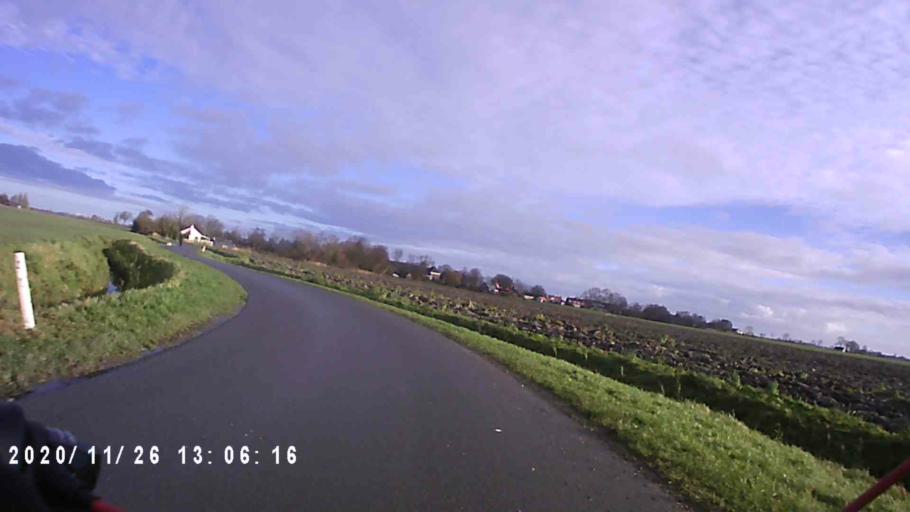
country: NL
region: Groningen
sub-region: Gemeente Appingedam
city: Appingedam
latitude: 53.3523
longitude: 6.8429
